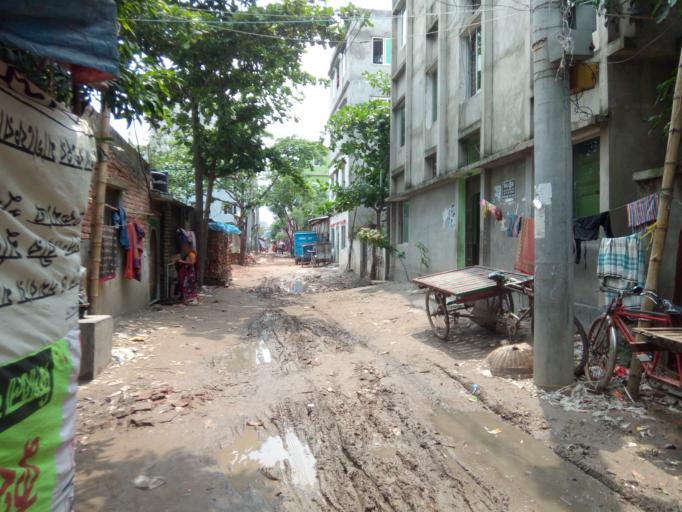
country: BD
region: Dhaka
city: Azimpur
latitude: 23.7557
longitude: 90.3527
